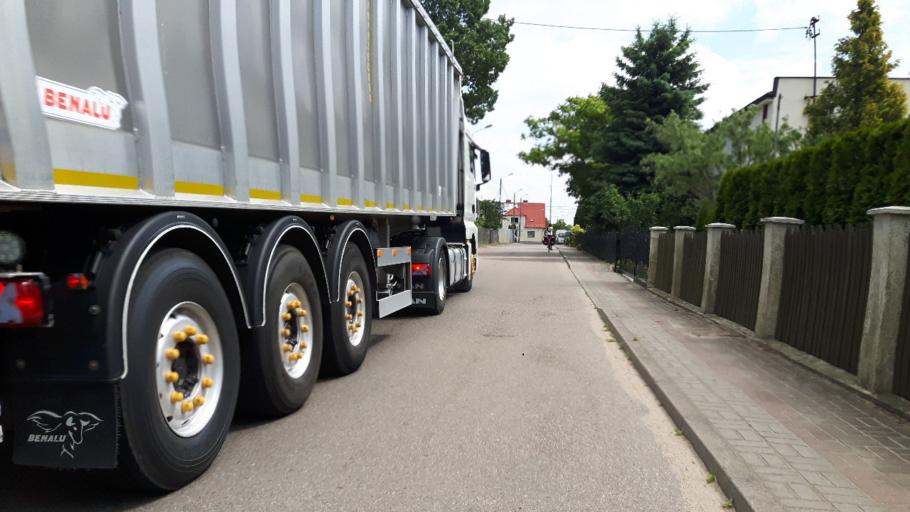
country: PL
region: Pomeranian Voivodeship
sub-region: Powiat wejherowski
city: Choczewo
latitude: 54.7415
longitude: 17.8894
